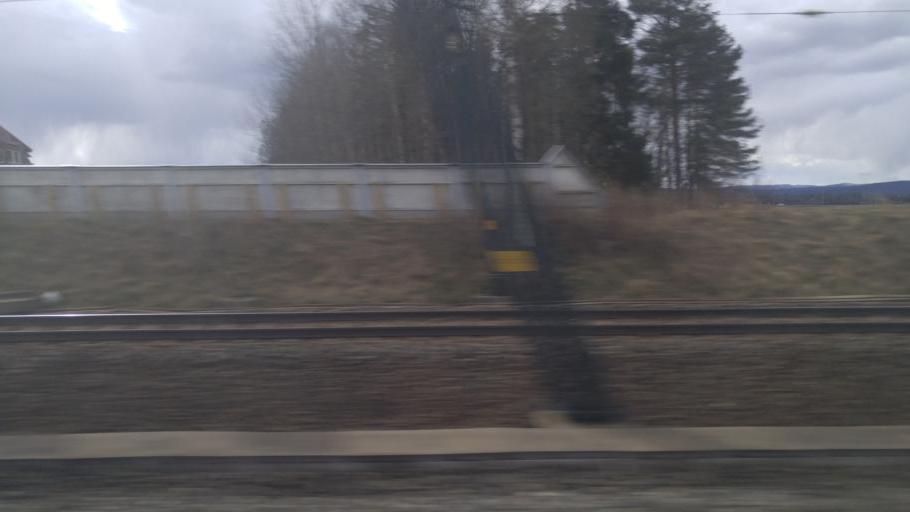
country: NO
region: Akershus
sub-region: Ullensaker
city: Klofta
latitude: 60.0855
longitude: 11.1402
